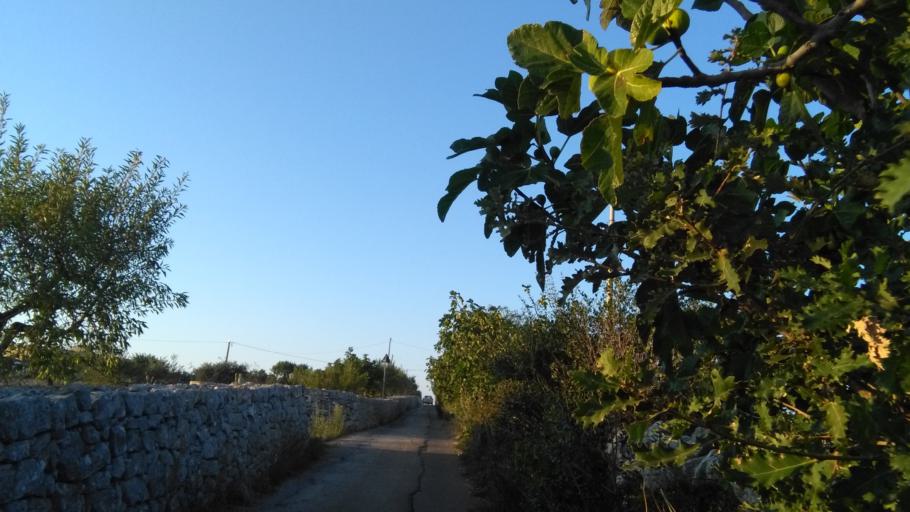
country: IT
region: Apulia
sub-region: Provincia di Bari
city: Putignano
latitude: 40.8234
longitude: 17.1028
